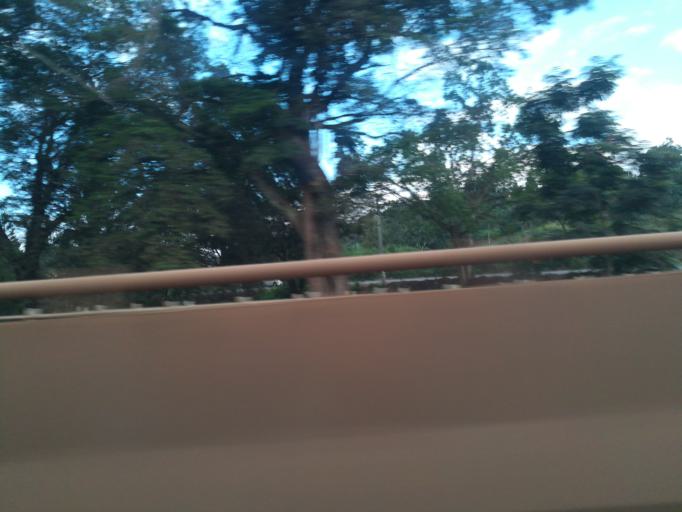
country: KE
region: Nairobi Area
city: Thika
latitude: -1.0269
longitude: 37.0655
